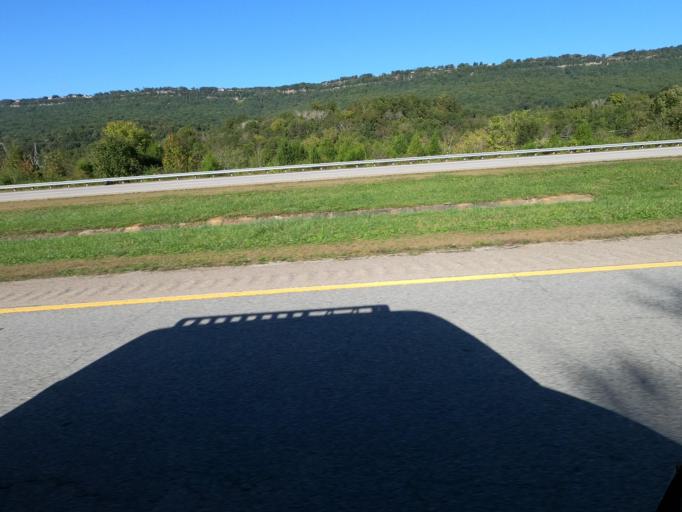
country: US
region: Tennessee
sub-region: Hamilton County
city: Walden
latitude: 35.1415
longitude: -85.2930
